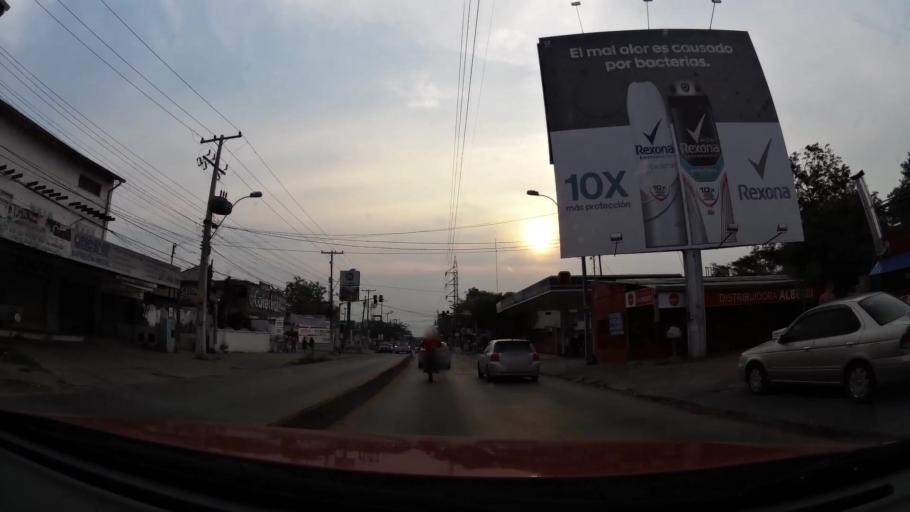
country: PY
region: Central
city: Lambare
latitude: -25.3402
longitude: -57.5990
